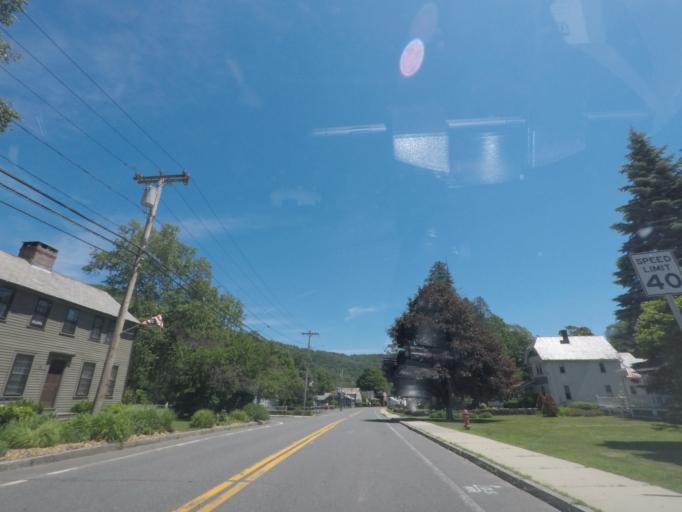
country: US
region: Massachusetts
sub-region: Berkshire County
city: Becket
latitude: 42.2777
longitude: -72.9793
